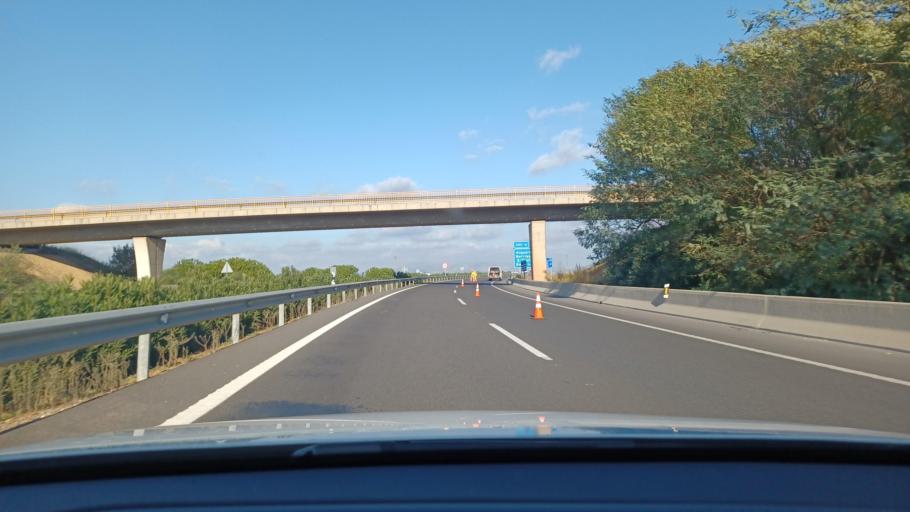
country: ES
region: Valencia
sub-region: Provincia de Castello
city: Betxi
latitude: 39.9210
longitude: -0.1952
